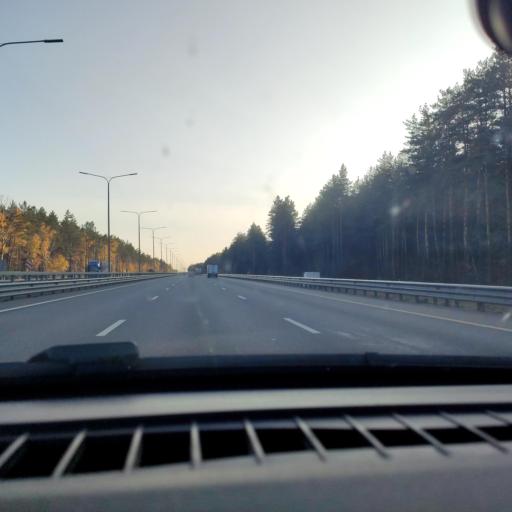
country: RU
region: Voronezj
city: Somovo
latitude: 51.7236
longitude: 39.3103
